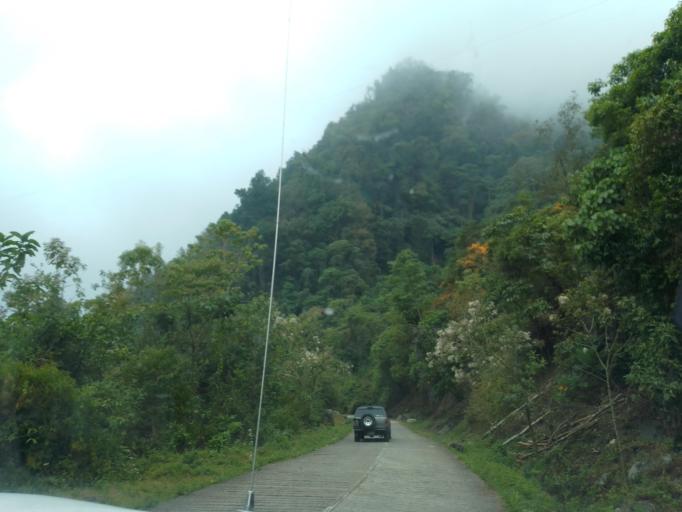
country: MX
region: Chiapas
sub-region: Union Juarez
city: Santo Domingo
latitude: 15.0933
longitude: -92.0955
